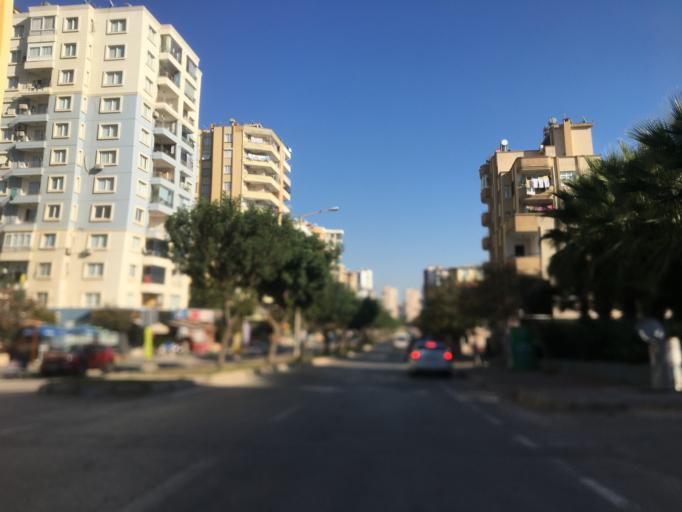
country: TR
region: Adana
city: Seyhan
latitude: 37.0290
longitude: 35.2671
